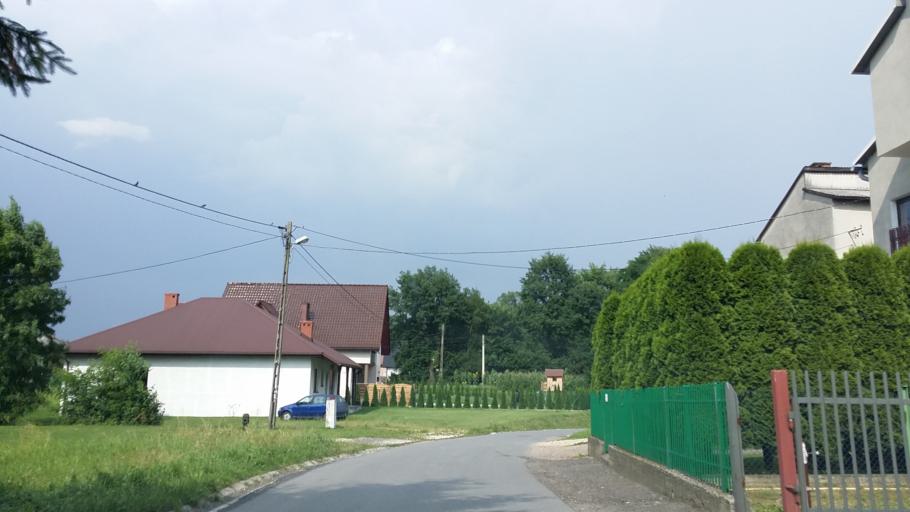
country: PL
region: Lesser Poland Voivodeship
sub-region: Powiat wadowicki
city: Spytkowice
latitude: 49.9976
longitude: 19.5156
